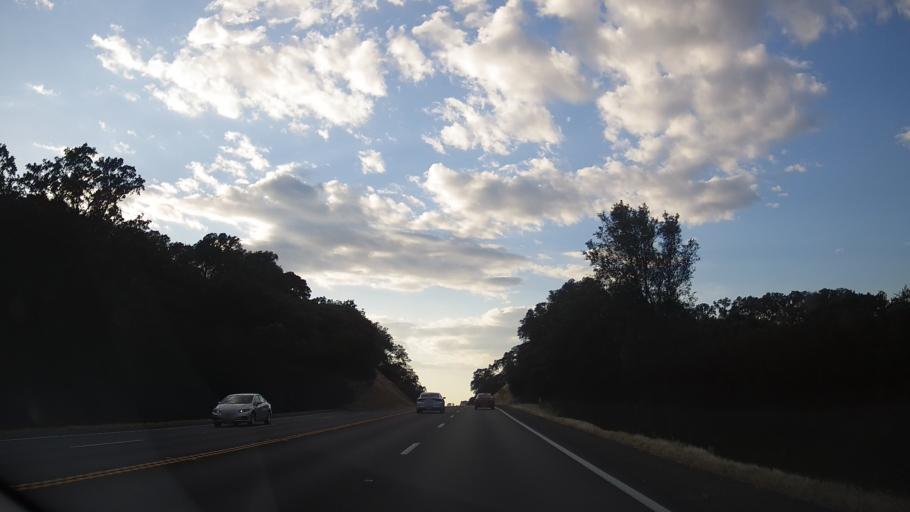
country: US
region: California
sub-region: Mendocino County
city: Talmage
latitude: 39.0086
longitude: -123.1231
